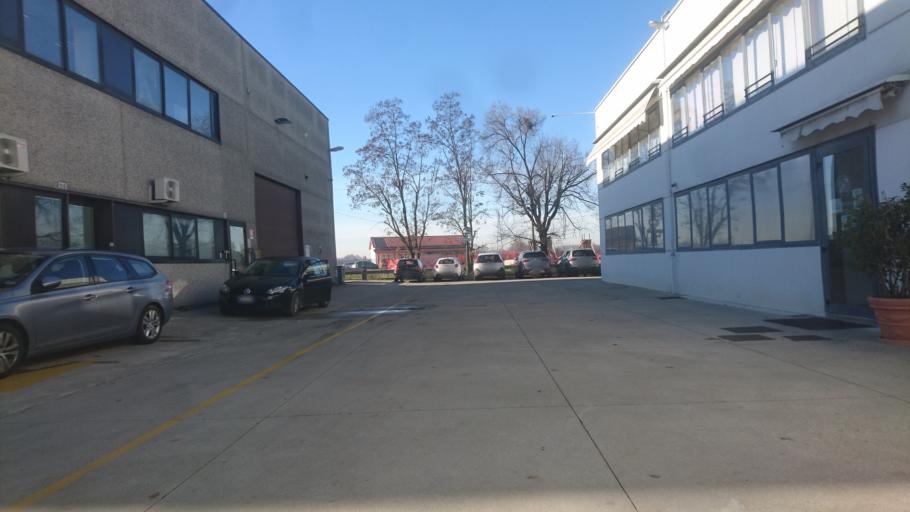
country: IT
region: Veneto
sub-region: Provincia di Padova
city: Limena
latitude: 45.4644
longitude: 11.8440
